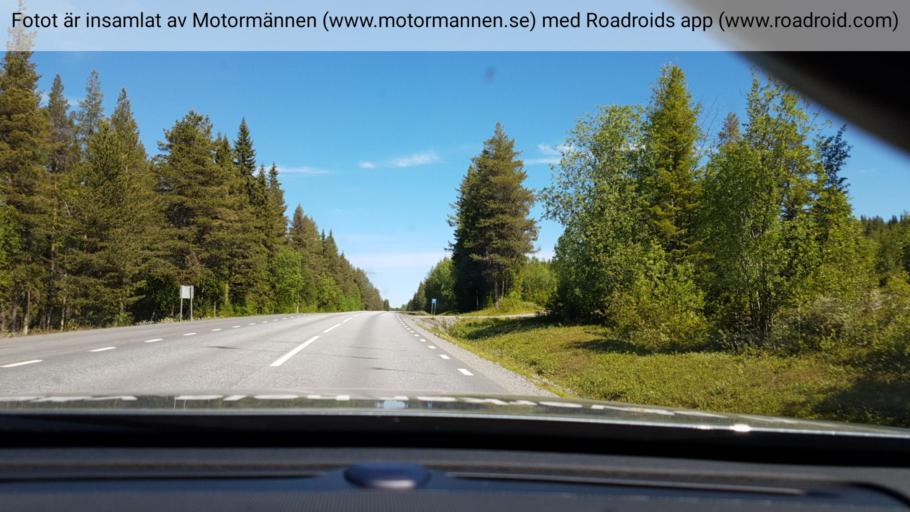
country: SE
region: Vaesterbotten
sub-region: Vilhelmina Kommun
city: Vilhelmina
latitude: 64.5606
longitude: 16.7408
